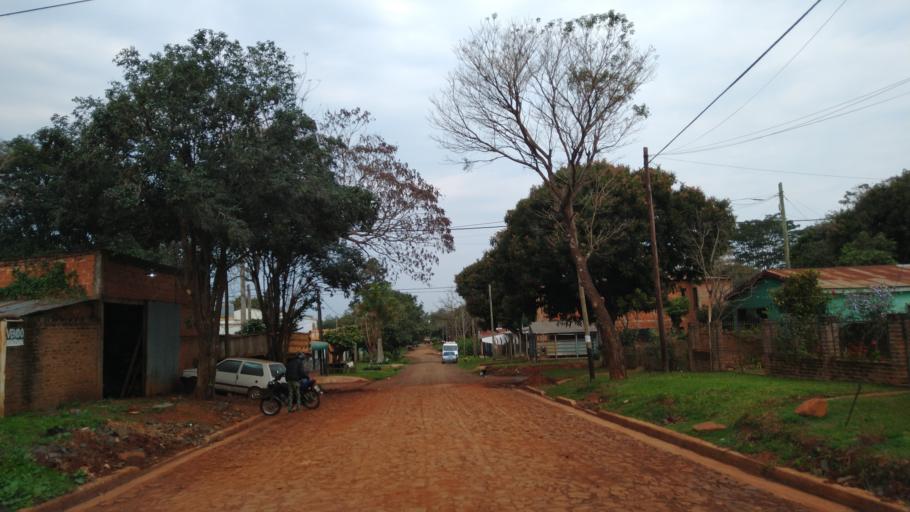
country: AR
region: Misiones
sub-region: Departamento de Capital
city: Posadas
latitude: -27.4323
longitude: -55.8816
